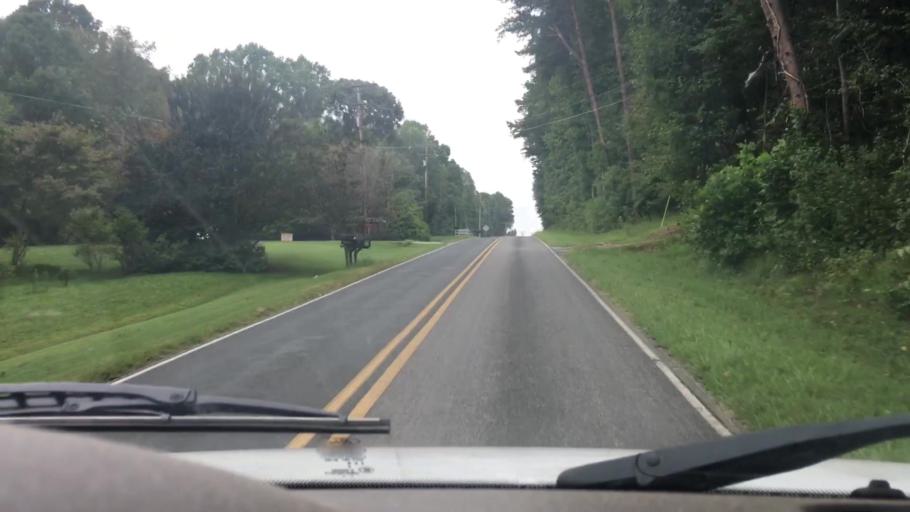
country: US
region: North Carolina
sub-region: Gaston County
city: Davidson
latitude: 35.5186
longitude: -80.8186
